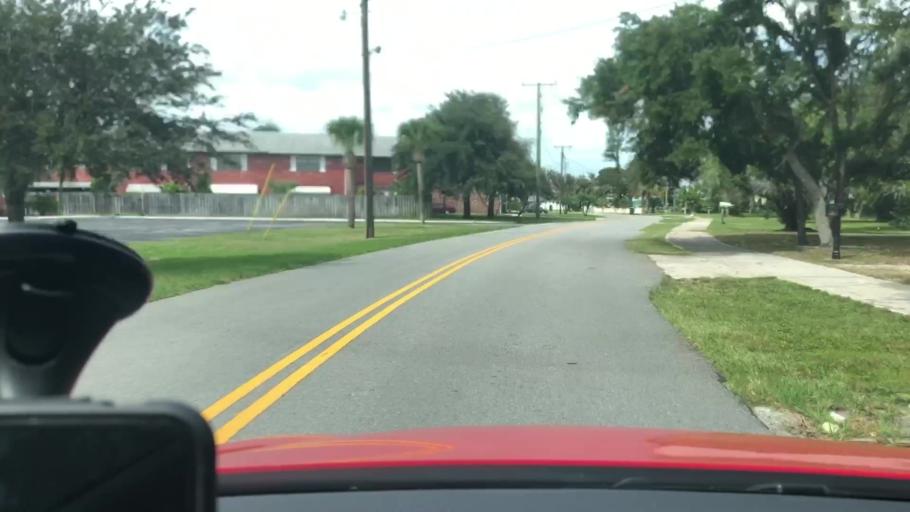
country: US
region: Florida
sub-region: Volusia County
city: South Daytona
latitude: 29.1691
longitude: -80.9992
